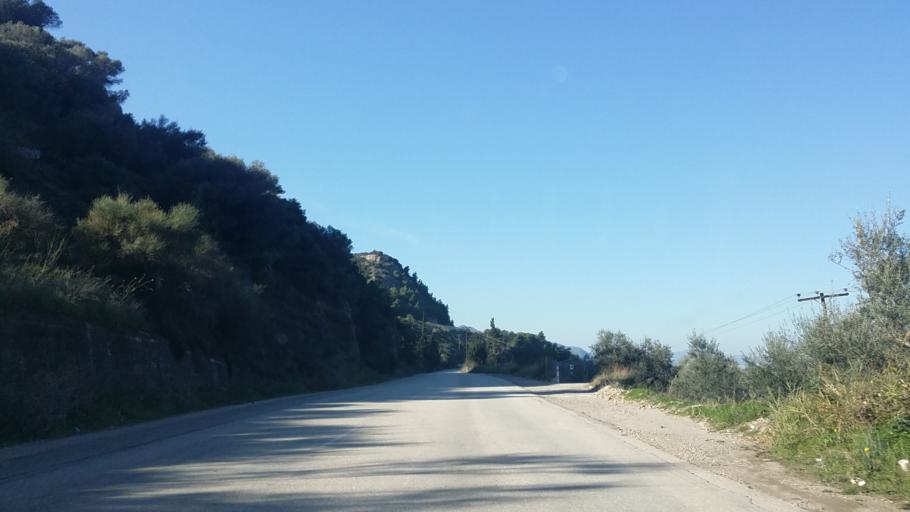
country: GR
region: West Greece
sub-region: Nomos Achaias
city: Akrata
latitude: 38.1789
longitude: 22.2202
